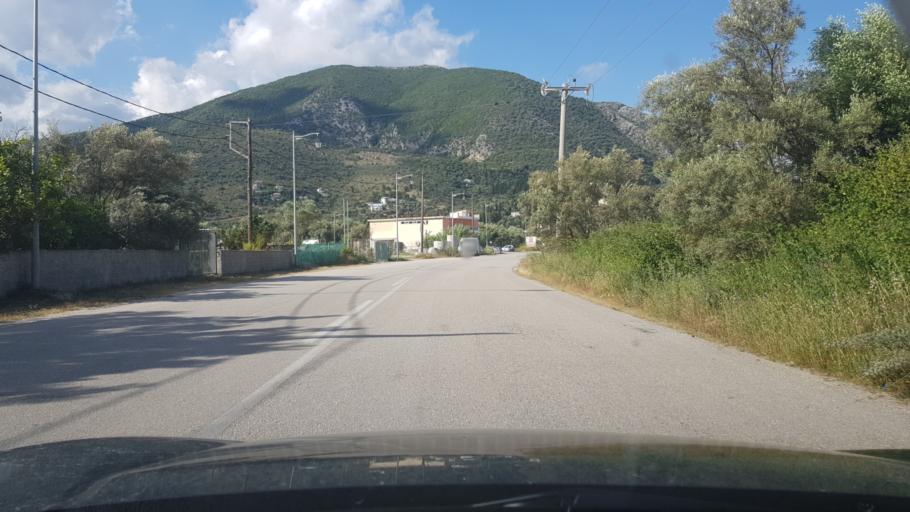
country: GR
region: Ionian Islands
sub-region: Lefkada
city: Nidri
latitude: 38.7079
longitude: 20.7044
